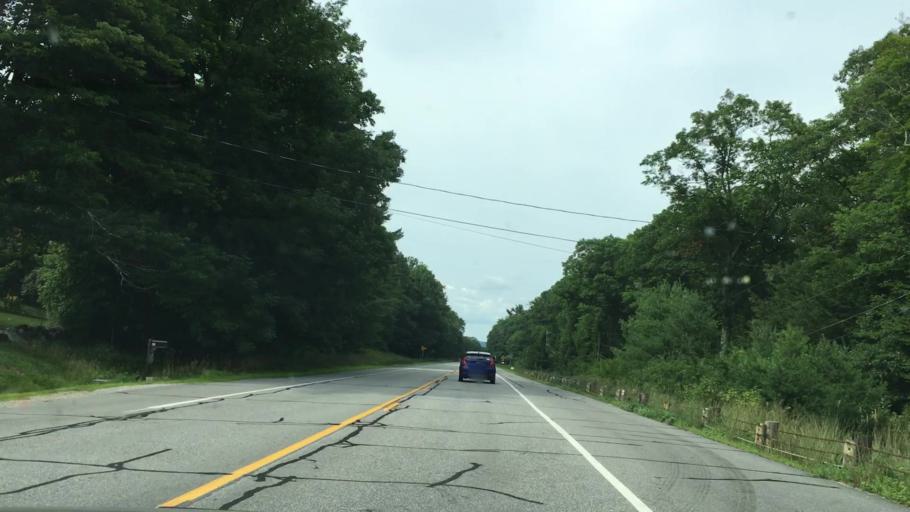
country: US
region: New Hampshire
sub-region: Hillsborough County
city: Antrim
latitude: 43.0680
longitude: -71.9157
